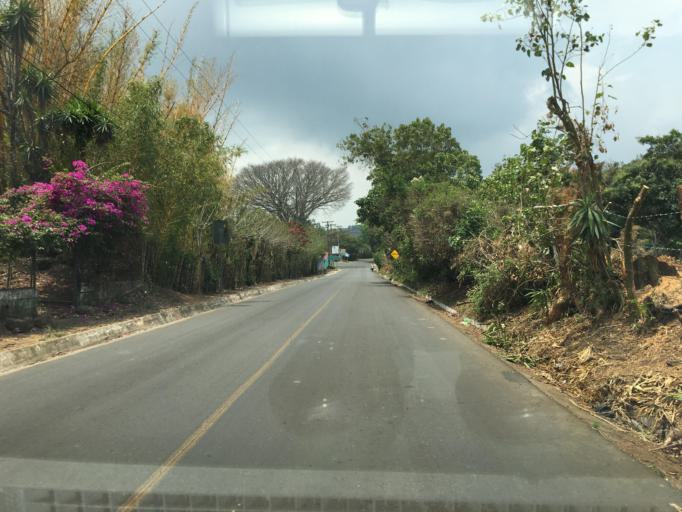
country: GT
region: Escuintla
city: San Vicente Pacaya
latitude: 14.3402
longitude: -90.5716
